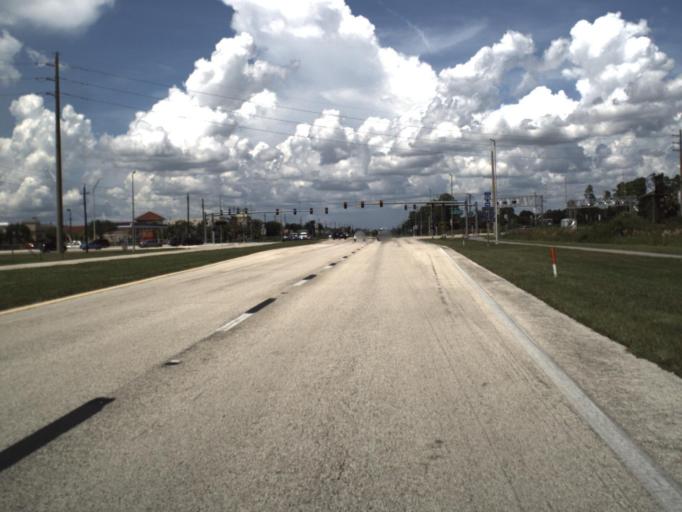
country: US
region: Florida
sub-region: Charlotte County
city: Charlotte Park
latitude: 26.8899
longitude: -82.0221
